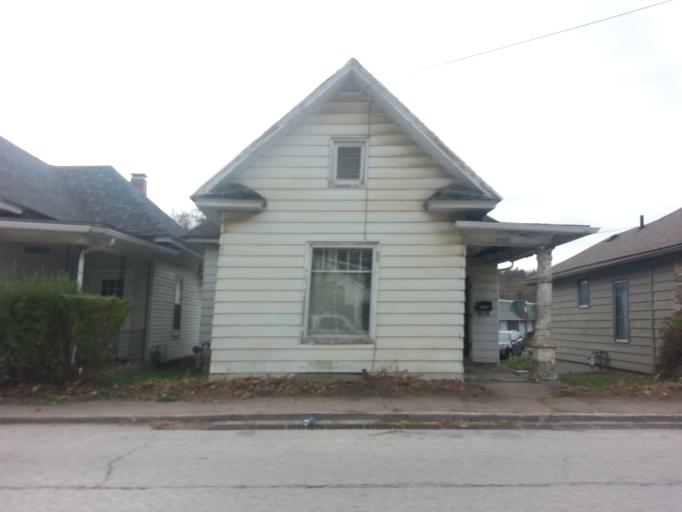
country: US
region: Missouri
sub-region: Marion County
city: Hannibal
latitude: 39.7053
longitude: -91.3857
